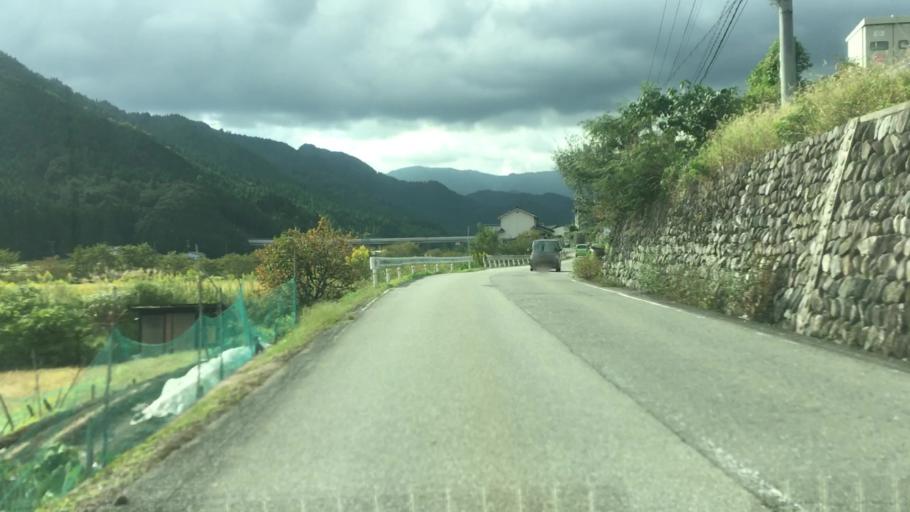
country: JP
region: Hyogo
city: Toyooka
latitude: 35.4094
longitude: 134.7502
